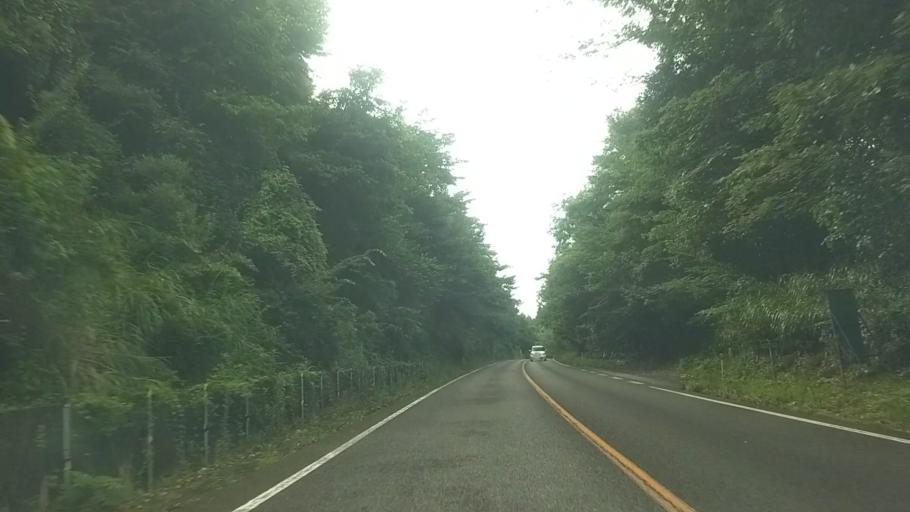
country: JP
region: Chiba
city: Kawaguchi
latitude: 35.2312
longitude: 140.0291
